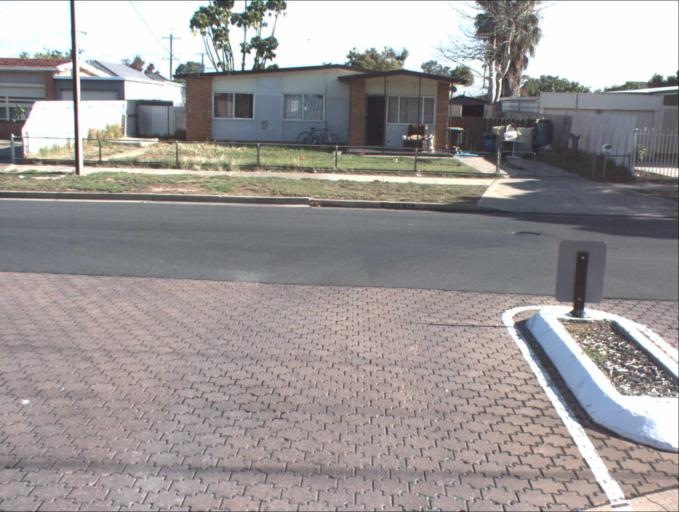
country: AU
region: South Australia
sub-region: Charles Sturt
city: Woodville North
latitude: -34.8588
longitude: 138.5518
